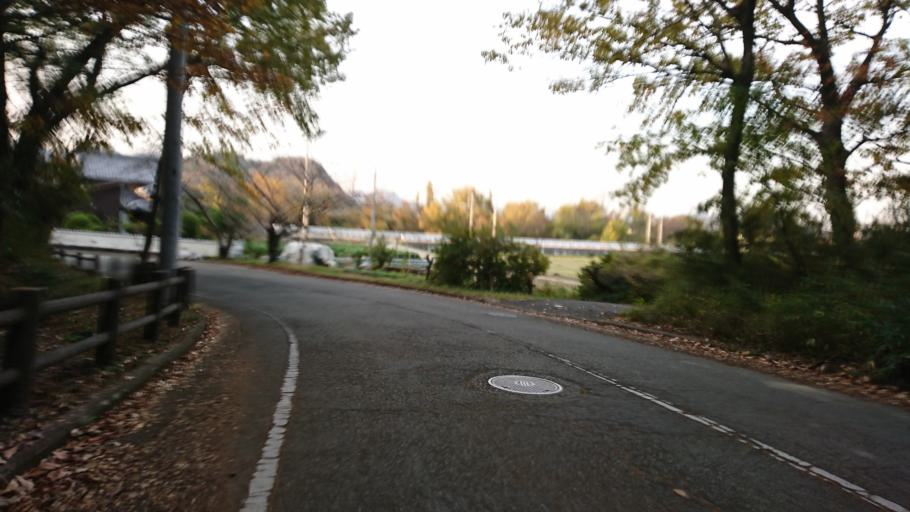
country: JP
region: Hyogo
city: Kakogawacho-honmachi
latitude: 34.7828
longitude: 134.8641
